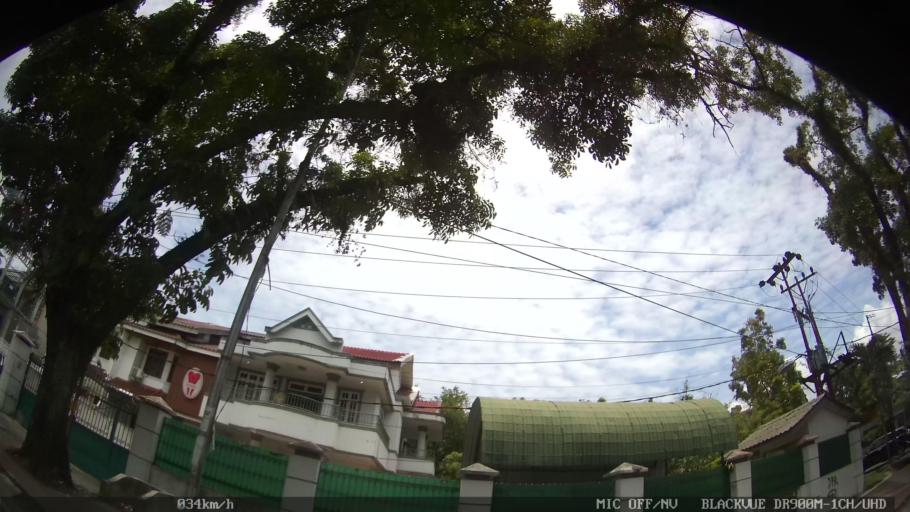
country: ID
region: North Sumatra
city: Medan
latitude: 3.5747
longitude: 98.6651
